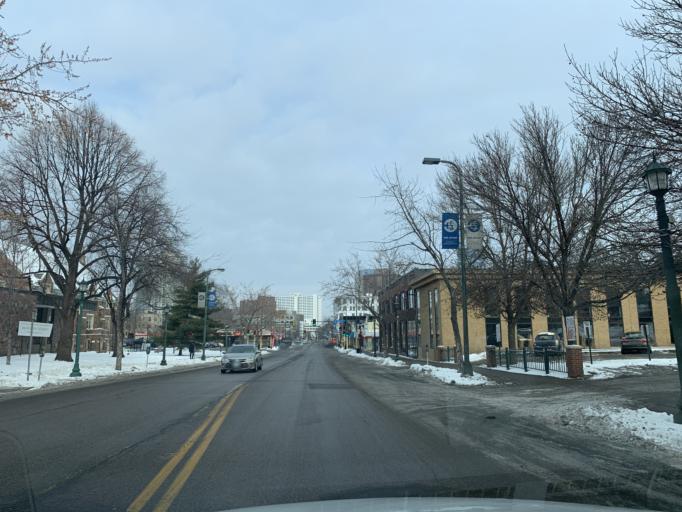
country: US
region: Minnesota
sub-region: Hennepin County
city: Minneapolis
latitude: 44.9631
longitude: -93.2777
